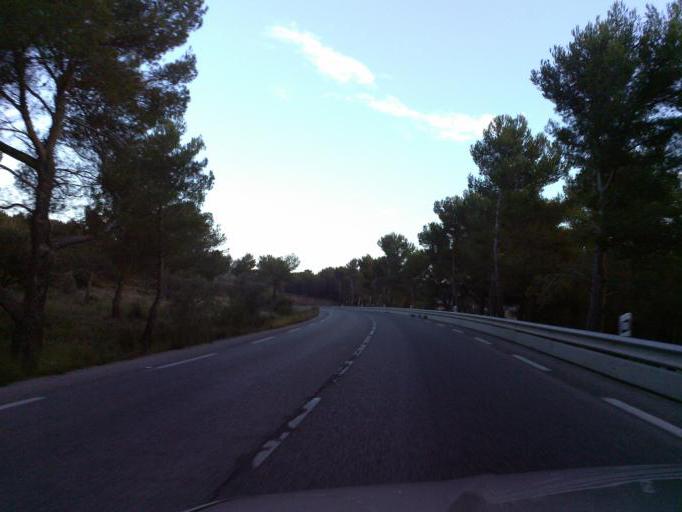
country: FR
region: Provence-Alpes-Cote d'Azur
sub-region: Departement des Bouches-du-Rhone
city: Lambesc
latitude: 43.6422
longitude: 5.2781
